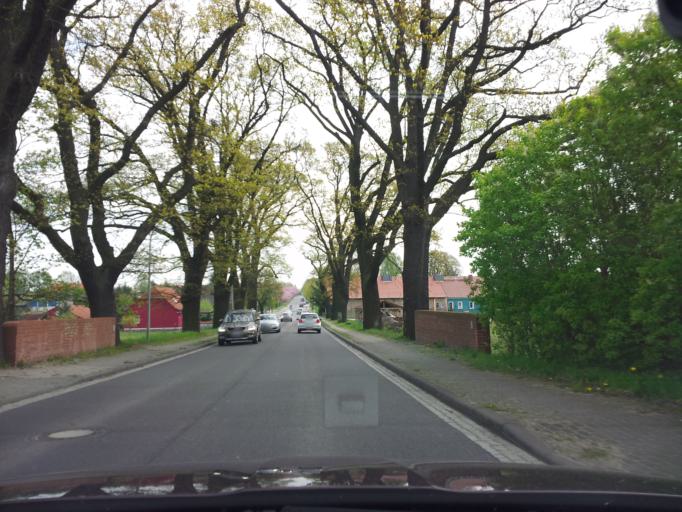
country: DE
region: Brandenburg
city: Lietzen
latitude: 52.5111
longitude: 14.3206
